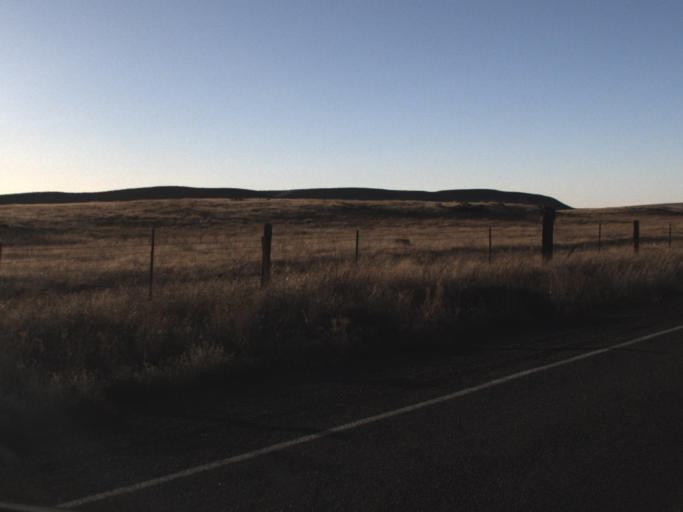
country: US
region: Washington
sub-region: Walla Walla County
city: Waitsburg
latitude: 46.6616
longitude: -118.2720
